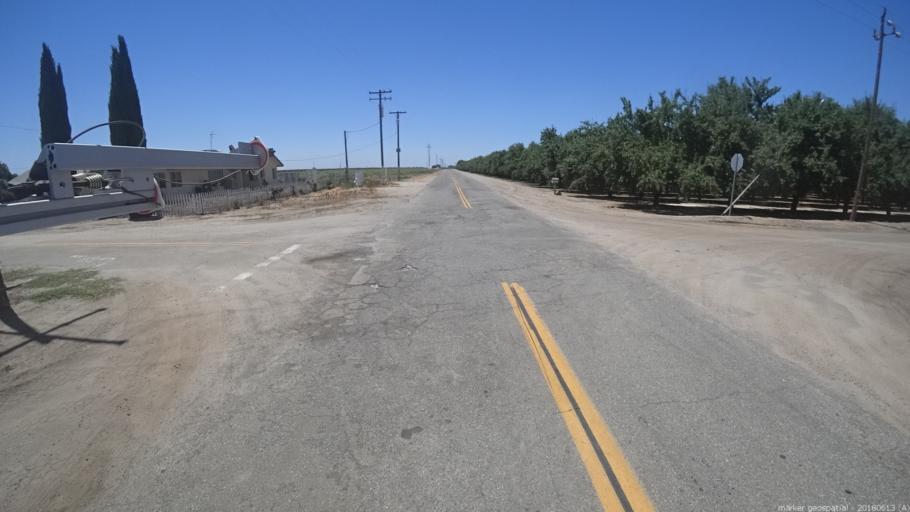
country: US
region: California
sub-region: Madera County
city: Fairmead
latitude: 36.9964
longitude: -120.2475
